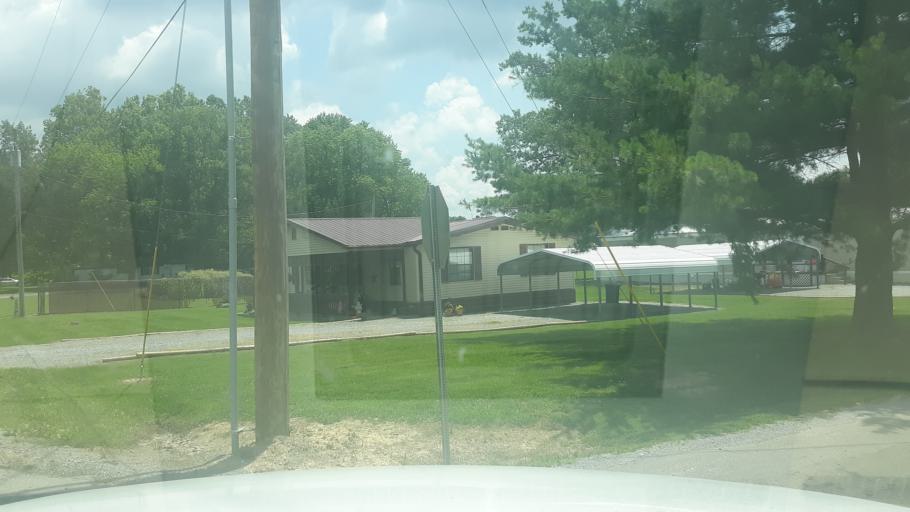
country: US
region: Illinois
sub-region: Saline County
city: Harrisburg
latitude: 37.8431
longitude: -88.6101
